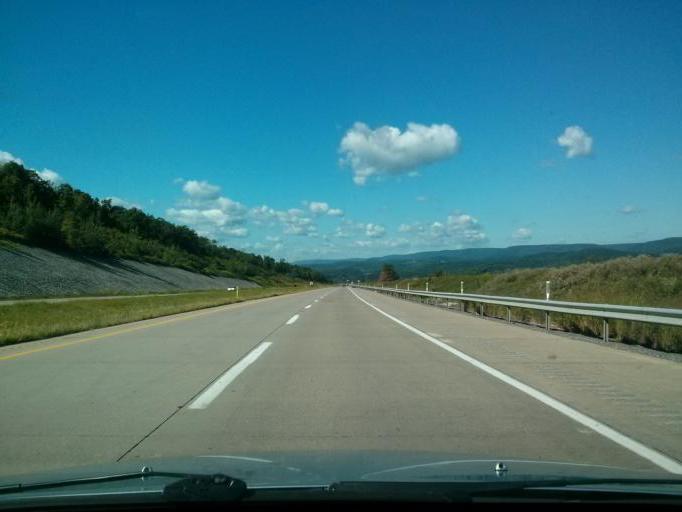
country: US
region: Pennsylvania
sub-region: Centre County
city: Stormstown
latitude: 40.8253
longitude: -77.9990
